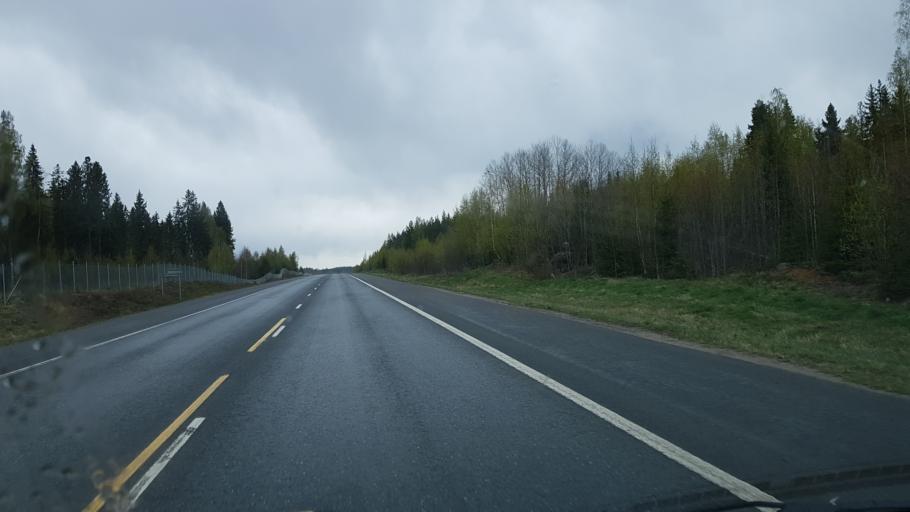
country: FI
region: Pirkanmaa
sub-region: Tampere
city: Pirkkala
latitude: 61.4116
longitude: 23.6340
